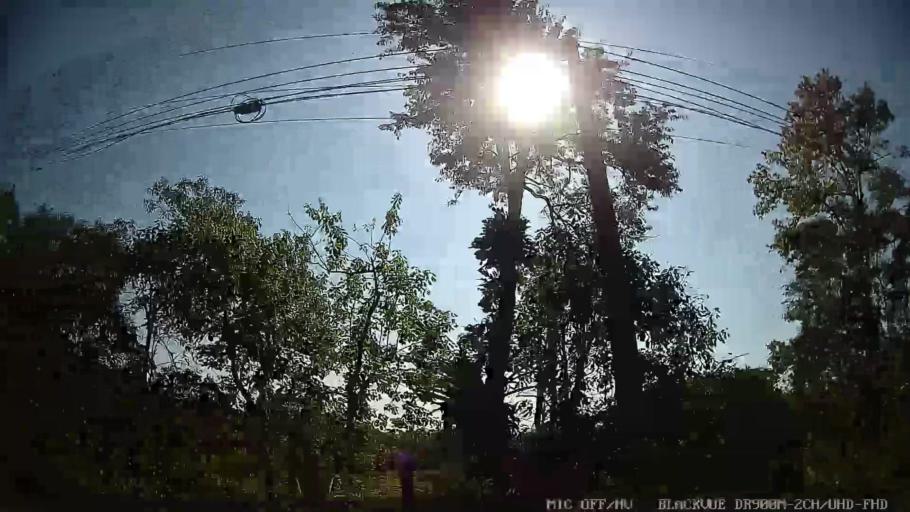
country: BR
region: Sao Paulo
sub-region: Guaruja
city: Guaruja
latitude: -24.0050
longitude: -46.3066
